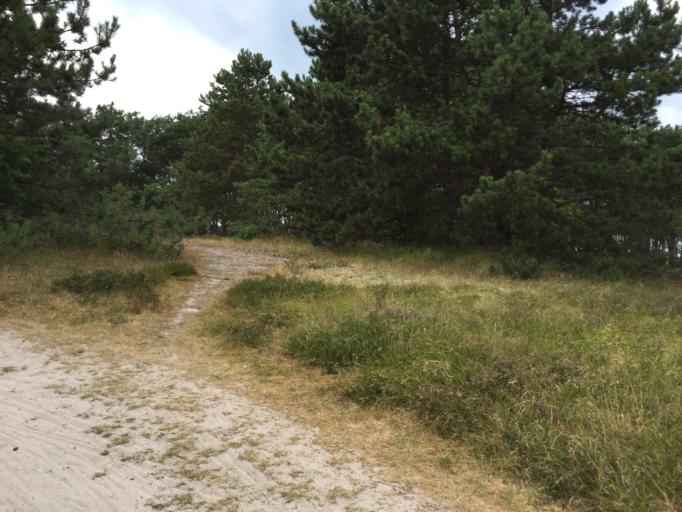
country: DE
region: Mecklenburg-Vorpommern
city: Hiddensee
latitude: 54.4912
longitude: 13.0685
